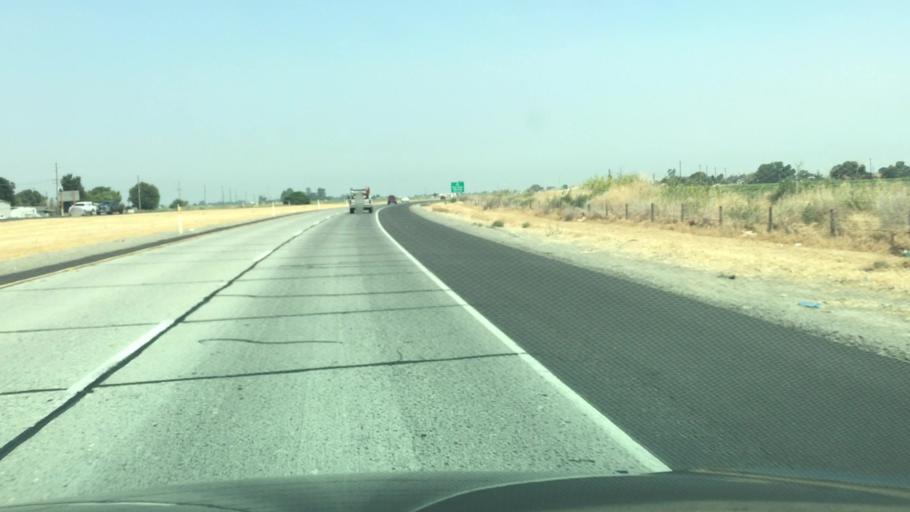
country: US
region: California
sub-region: Merced County
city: Dos Palos
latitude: 37.0539
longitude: -120.6492
